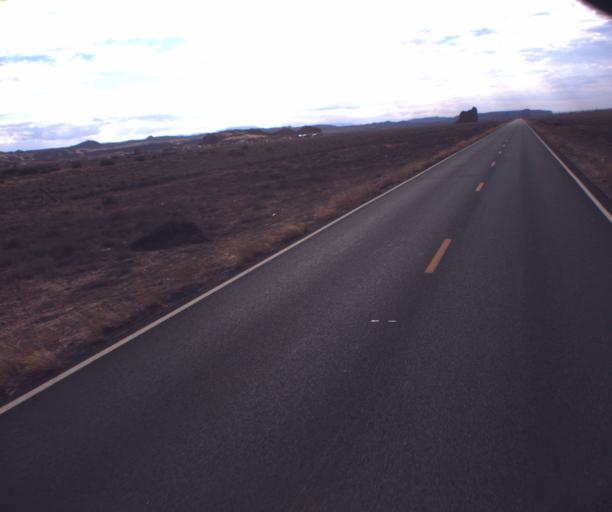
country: US
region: Arizona
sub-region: Apache County
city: Many Farms
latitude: 36.7585
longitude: -109.6486
